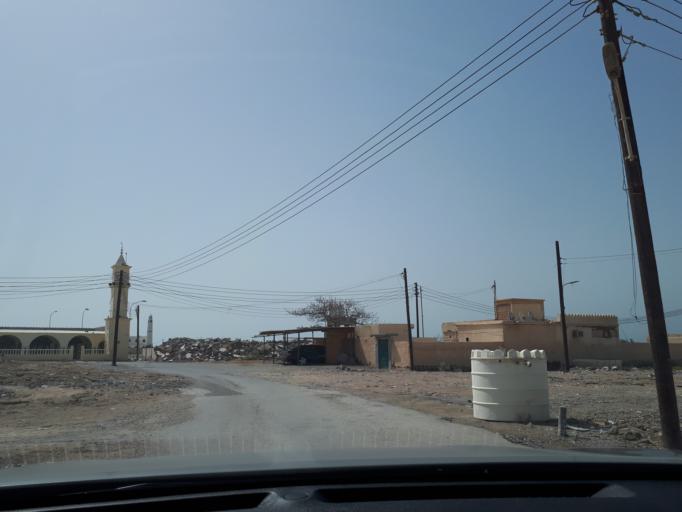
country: OM
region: Al Batinah
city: Barka'
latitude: 23.7084
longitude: 57.9032
